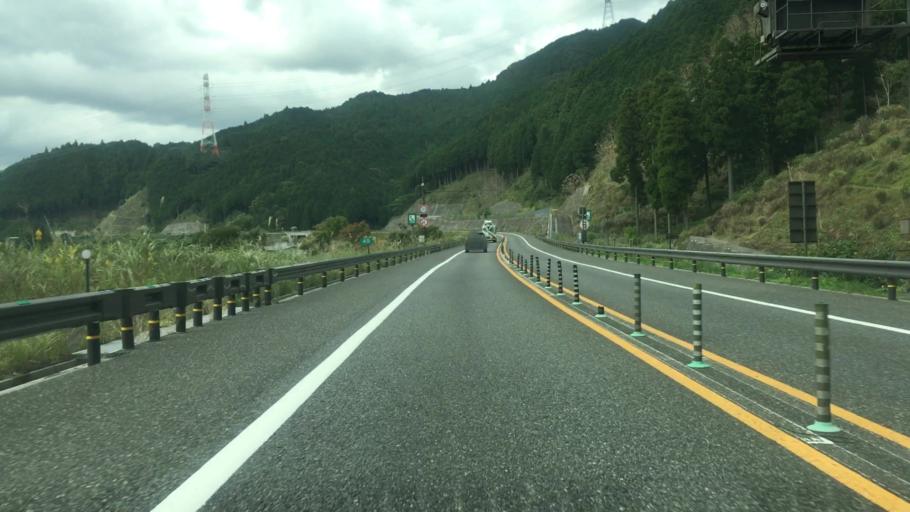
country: JP
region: Kyoto
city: Fukuchiyama
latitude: 35.2809
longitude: 134.9864
